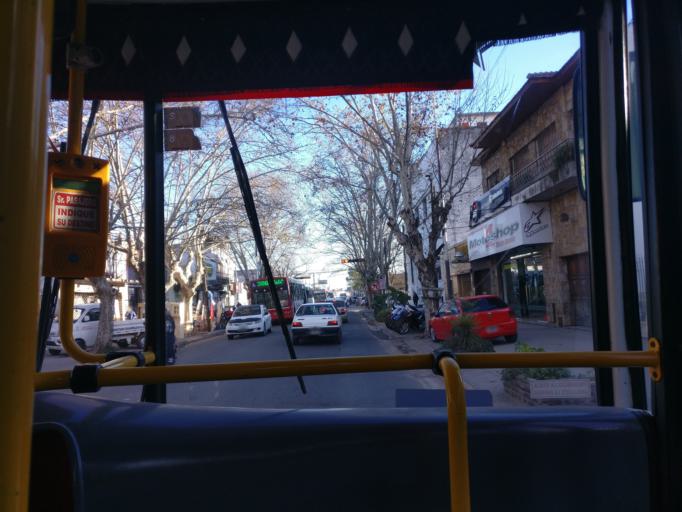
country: AR
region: Buenos Aires
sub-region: Partido de Ezeiza
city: Ezeiza
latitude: -34.8903
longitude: -58.5683
